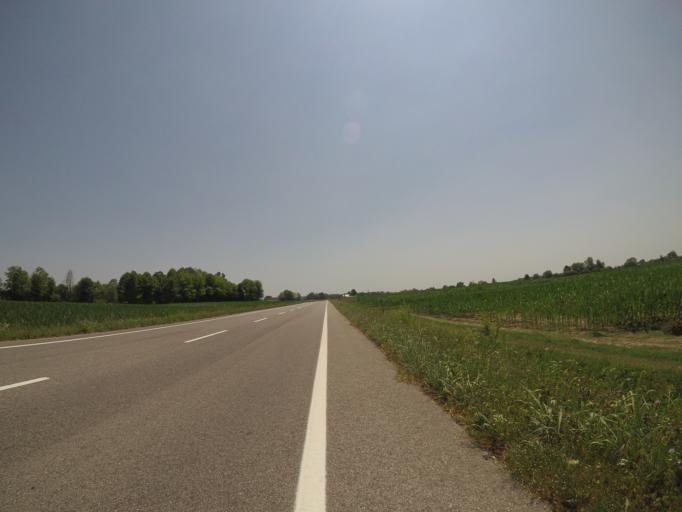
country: IT
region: Friuli Venezia Giulia
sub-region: Provincia di Udine
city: Varmo
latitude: 45.9016
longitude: 13.0056
